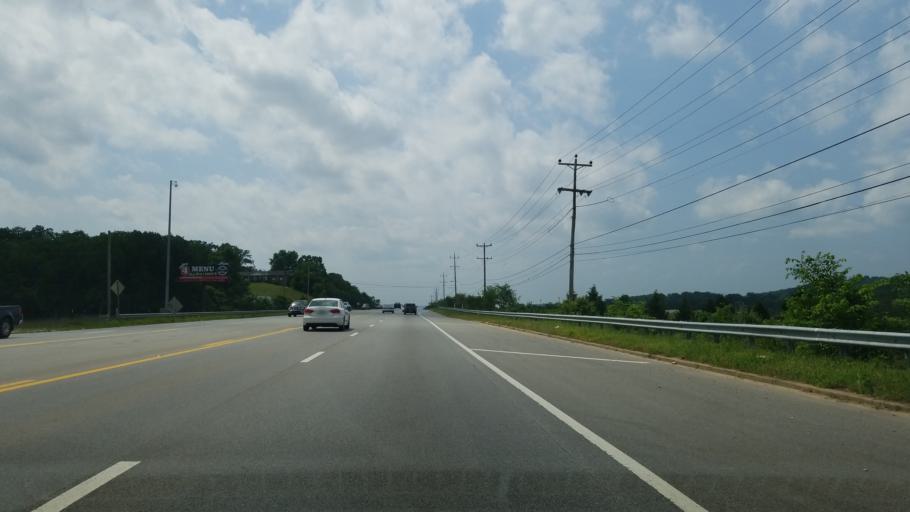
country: US
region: Tennessee
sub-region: Hamilton County
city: Falling Water
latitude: 35.1694
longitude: -85.2478
